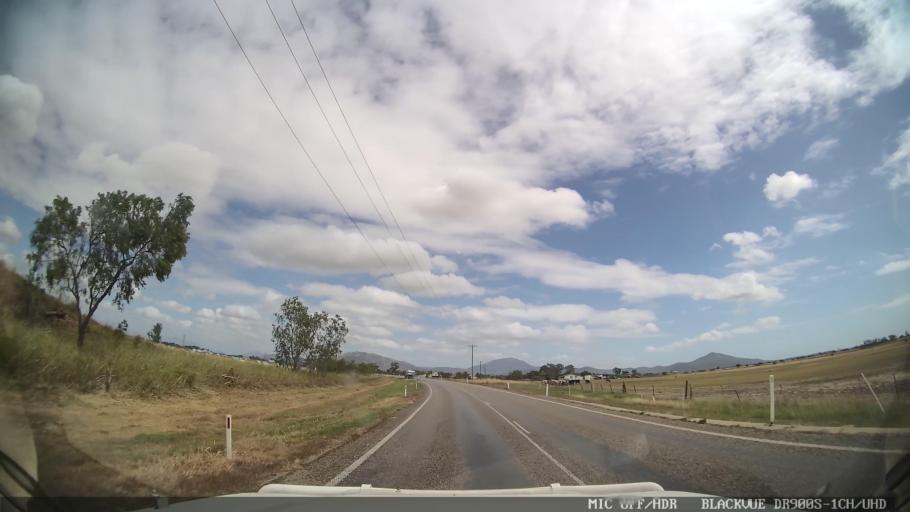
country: AU
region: Queensland
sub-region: Whitsunday
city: Bowen
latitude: -20.0150
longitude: 148.1771
